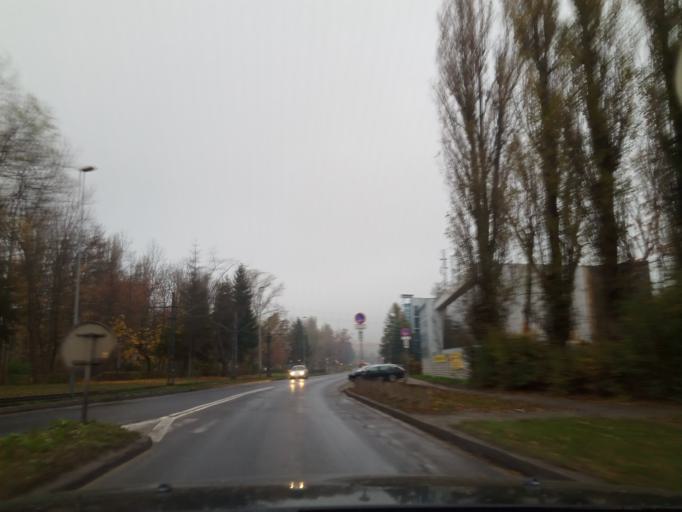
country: PL
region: Lesser Poland Voivodeship
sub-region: Powiat wielicki
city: Kokotow
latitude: 50.0821
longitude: 20.0660
